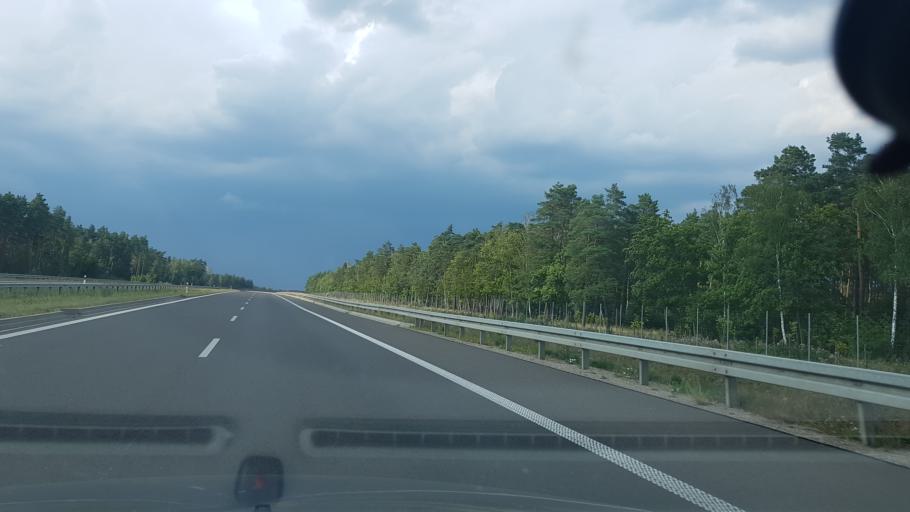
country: PL
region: Masovian Voivodeship
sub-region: Powiat mlawski
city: Wieczfnia Koscielna
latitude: 53.2446
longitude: 20.4243
